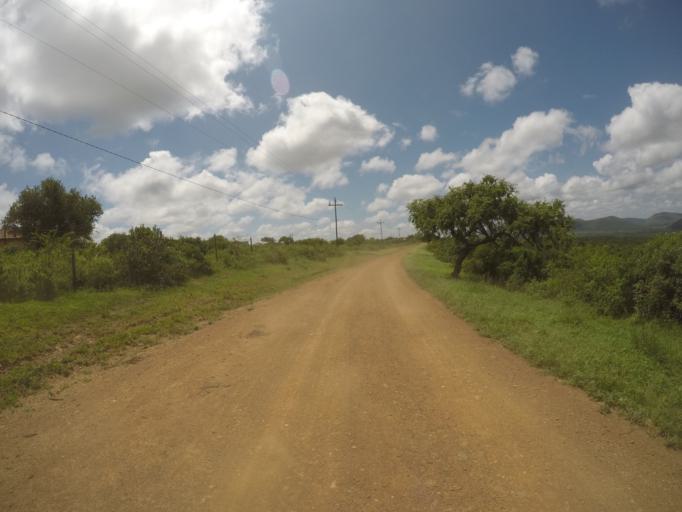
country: ZA
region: KwaZulu-Natal
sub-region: uThungulu District Municipality
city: Empangeni
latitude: -28.5868
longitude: 31.8221
